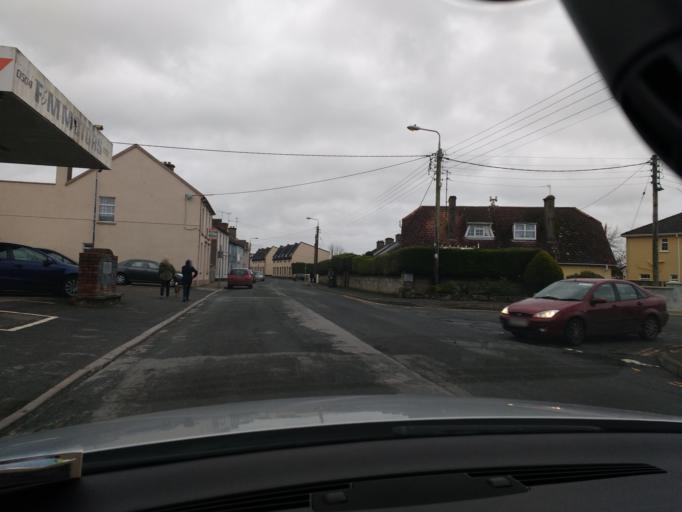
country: IE
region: Munster
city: Thurles
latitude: 52.6754
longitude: -7.8168
